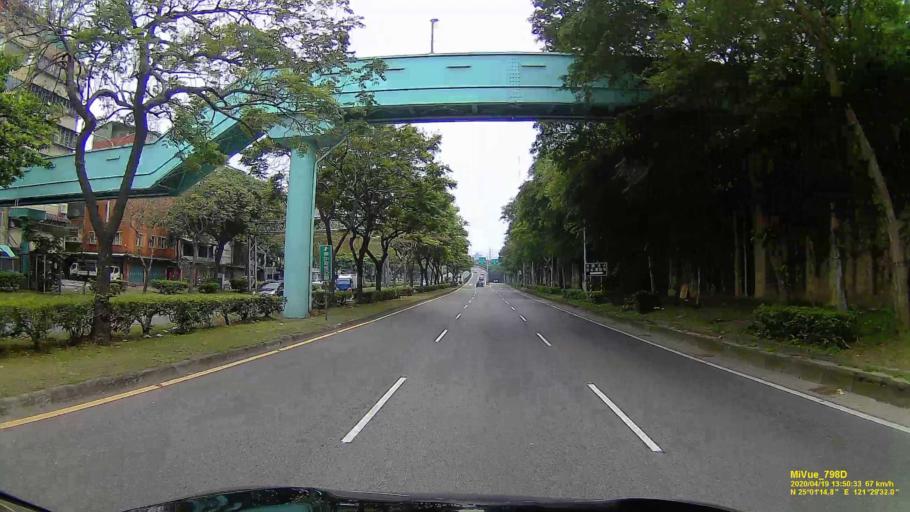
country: TW
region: Taipei
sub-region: Taipei
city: Banqiao
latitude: 25.0204
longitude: 121.4924
